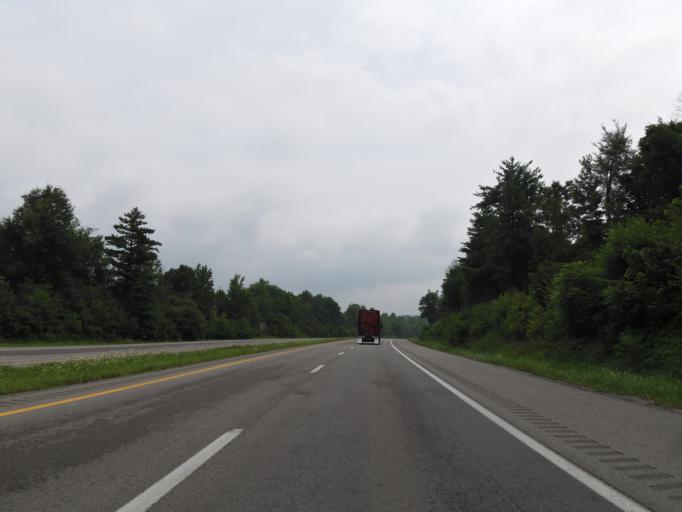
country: US
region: Kentucky
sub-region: Muhlenberg County
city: Central City
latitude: 37.3137
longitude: -87.0538
